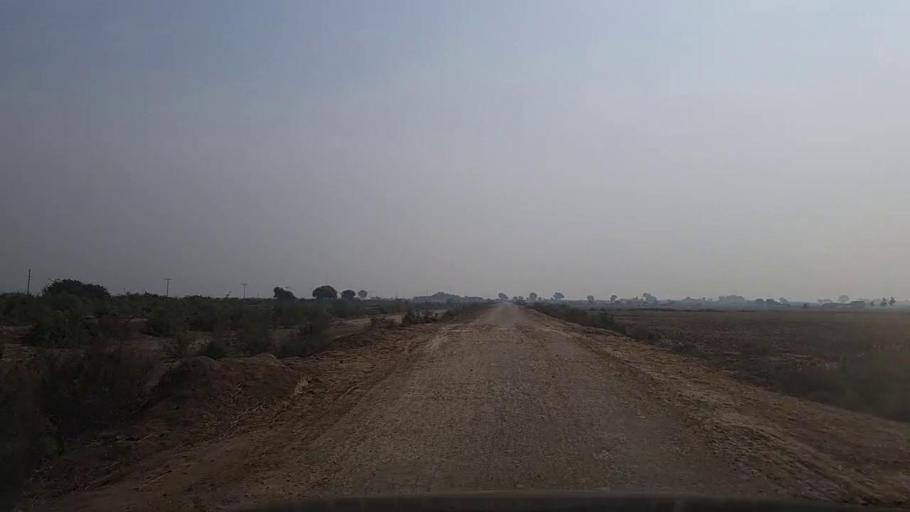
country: PK
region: Sindh
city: Mirpur Sakro
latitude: 24.3821
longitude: 67.7537
